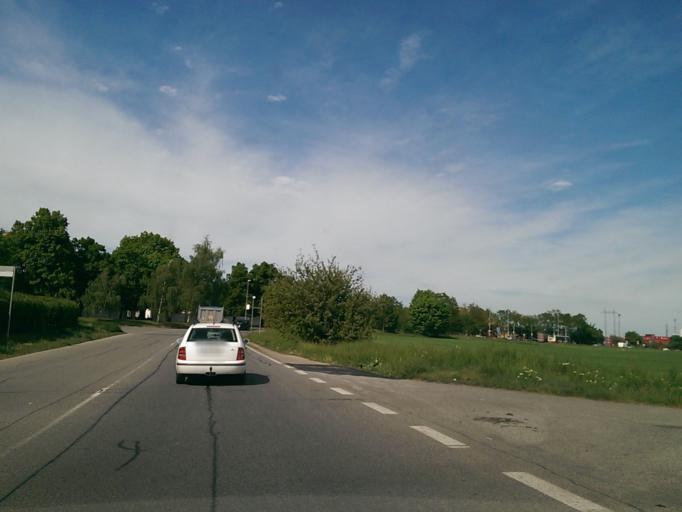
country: CZ
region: Central Bohemia
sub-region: Okres Praha-Zapad
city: Pruhonice
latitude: 50.0347
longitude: 14.5645
